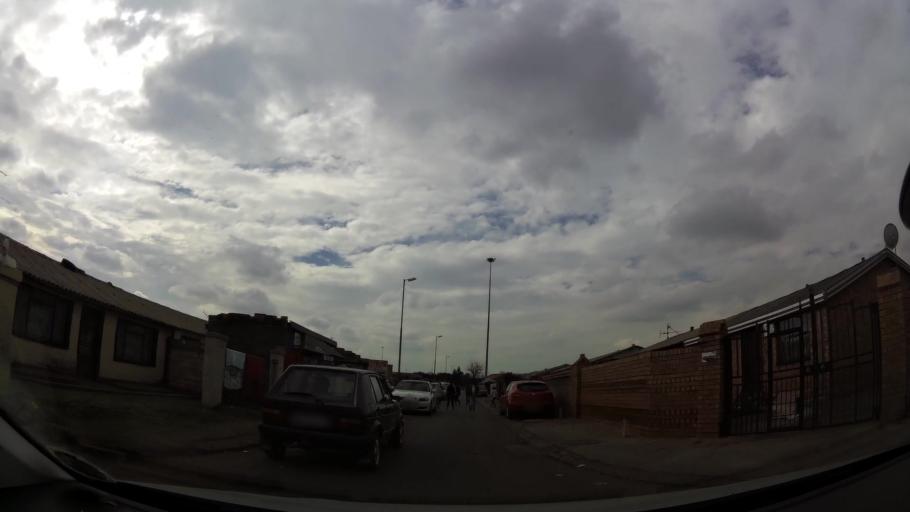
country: ZA
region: Gauteng
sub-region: City of Johannesburg Metropolitan Municipality
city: Soweto
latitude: -26.2739
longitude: 27.8533
